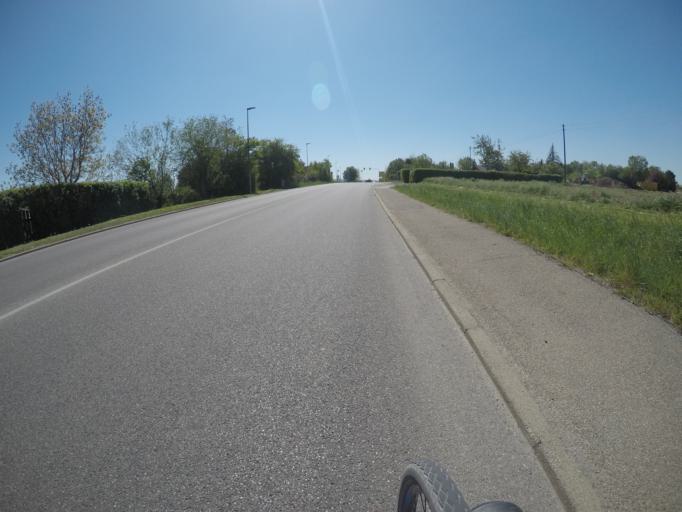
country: DE
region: Baden-Wuerttemberg
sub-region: Regierungsbezirk Stuttgart
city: Stuttgart Muehlhausen
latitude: 48.8280
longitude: 9.2547
